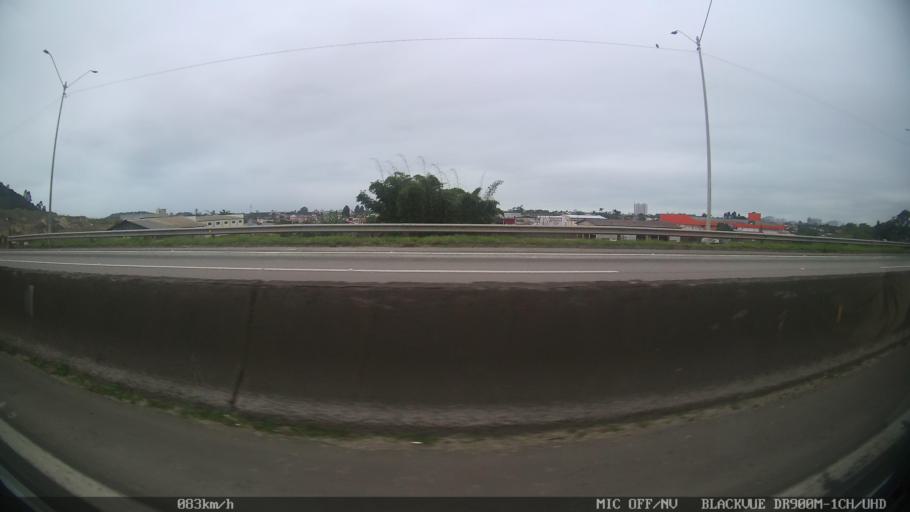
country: BR
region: Santa Catarina
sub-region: Penha
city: Penha
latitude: -26.7166
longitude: -48.7020
